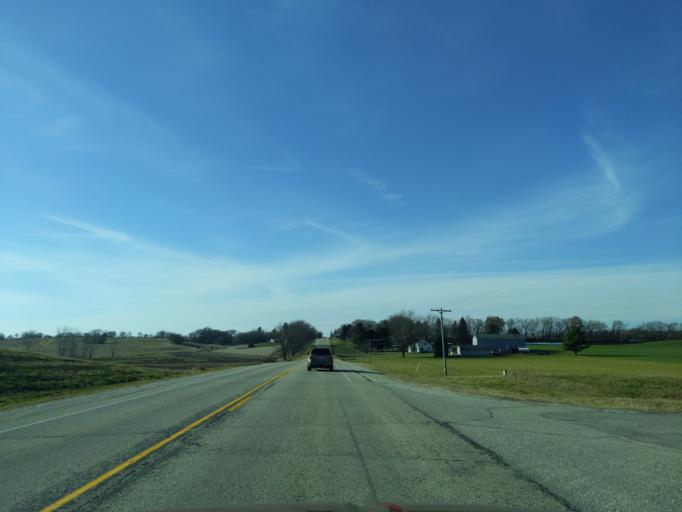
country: US
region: Wisconsin
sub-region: Jefferson County
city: Fort Atkinson
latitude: 42.8289
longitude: -88.8365
